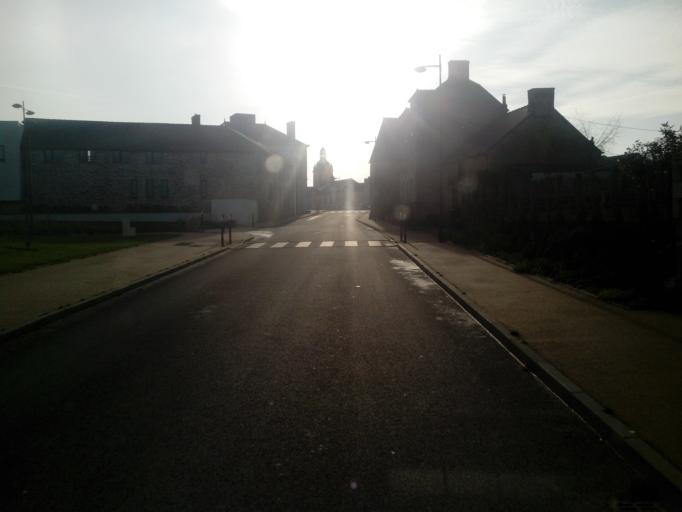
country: FR
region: Brittany
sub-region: Departement du Morbihan
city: Mauron
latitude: 48.0846
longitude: -2.2835
